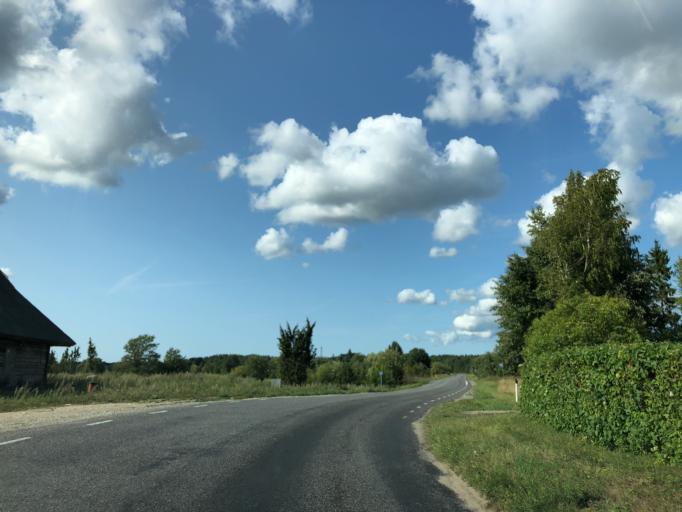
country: EE
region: Hiiumaa
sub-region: Kaerdla linn
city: Kardla
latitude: 58.8016
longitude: 22.7475
